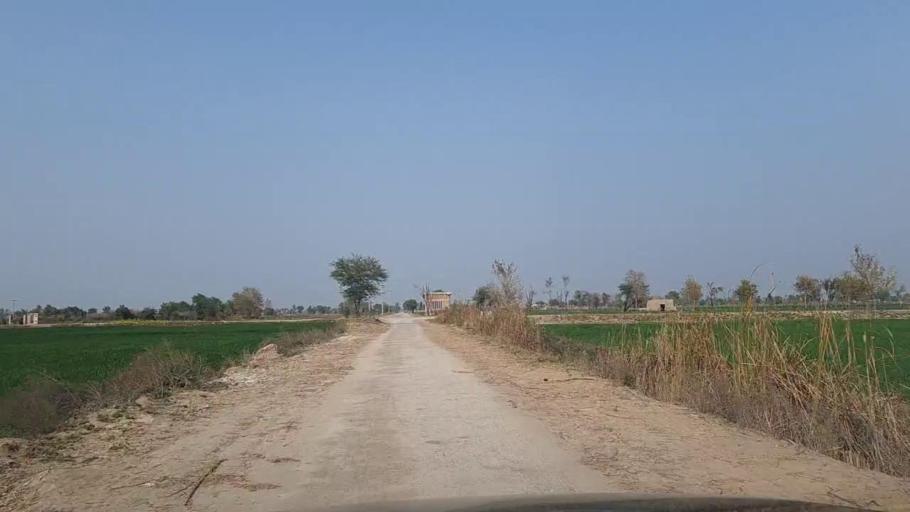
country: PK
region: Sindh
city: Daur
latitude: 26.4035
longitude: 68.4239
